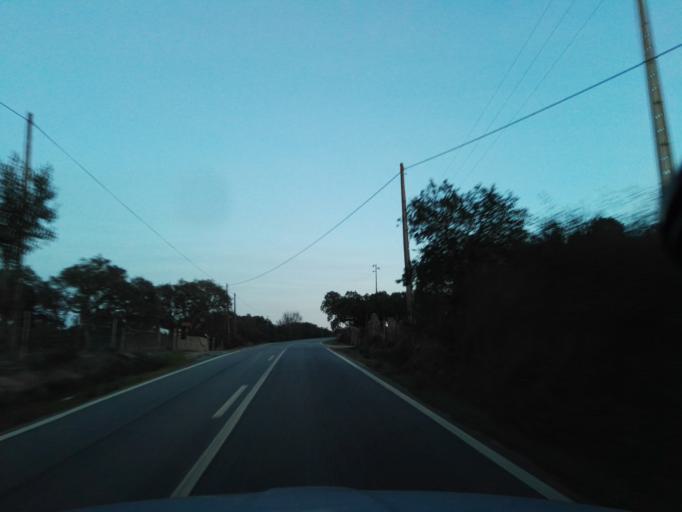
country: PT
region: Evora
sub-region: Arraiolos
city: Arraiolos
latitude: 38.7524
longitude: -8.0936
